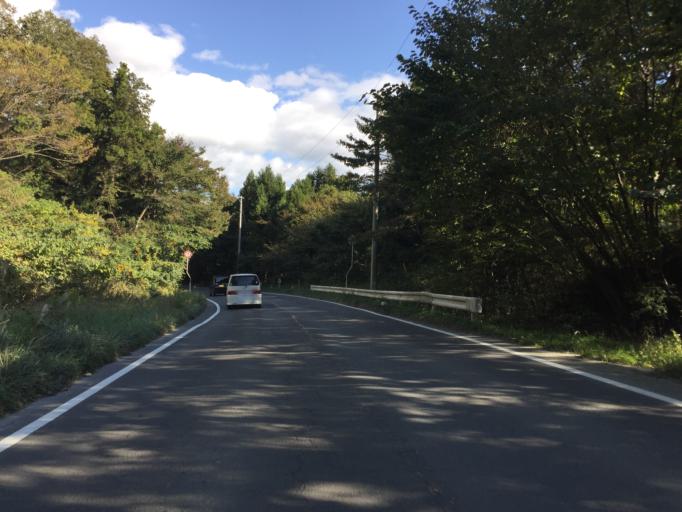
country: JP
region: Miyagi
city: Marumori
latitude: 37.8497
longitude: 140.8558
